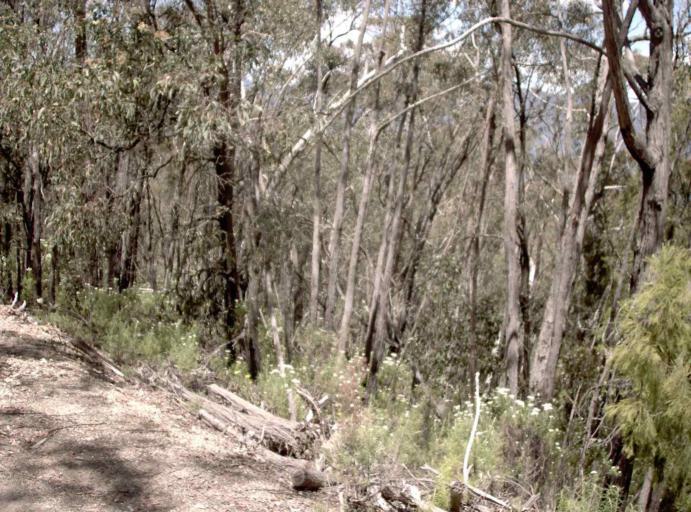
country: AU
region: New South Wales
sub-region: Snowy River
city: Jindabyne
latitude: -37.0842
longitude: 148.3327
